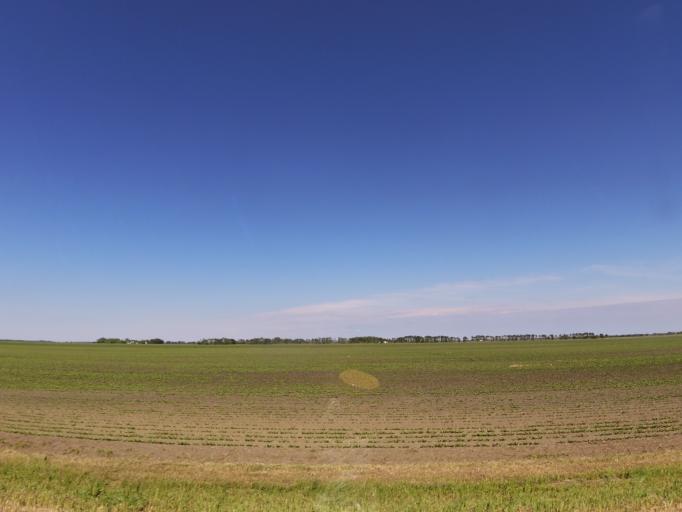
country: US
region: North Dakota
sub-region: Walsh County
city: Grafton
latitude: 48.3432
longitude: -97.2558
